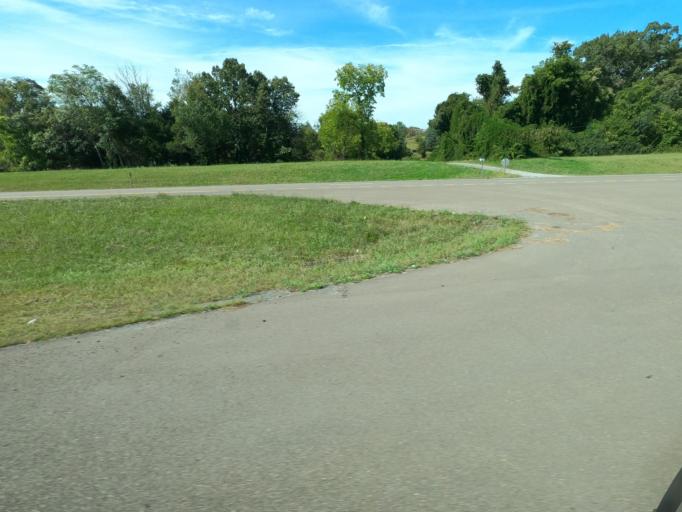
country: US
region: Tennessee
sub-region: Hamblen County
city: Morristown
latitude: 36.2764
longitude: -83.2819
